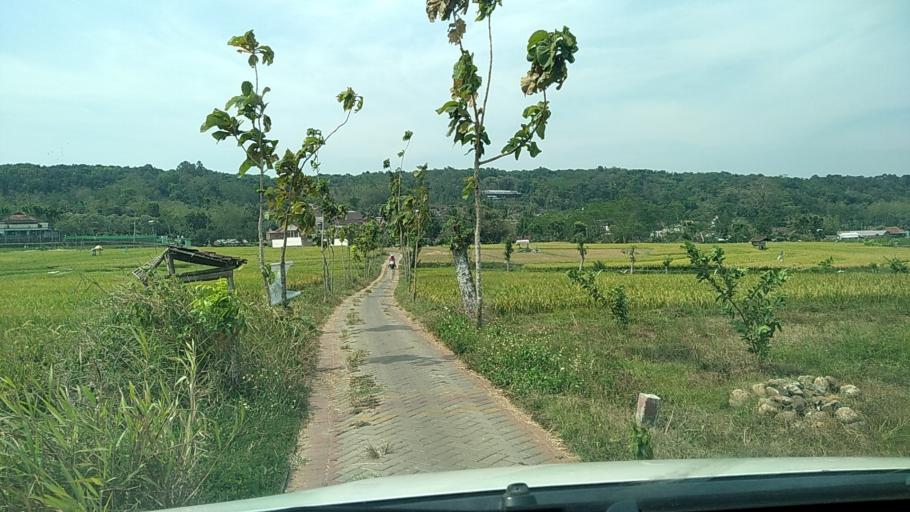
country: ID
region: Central Java
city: Ungaran
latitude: -7.0807
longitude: 110.3174
